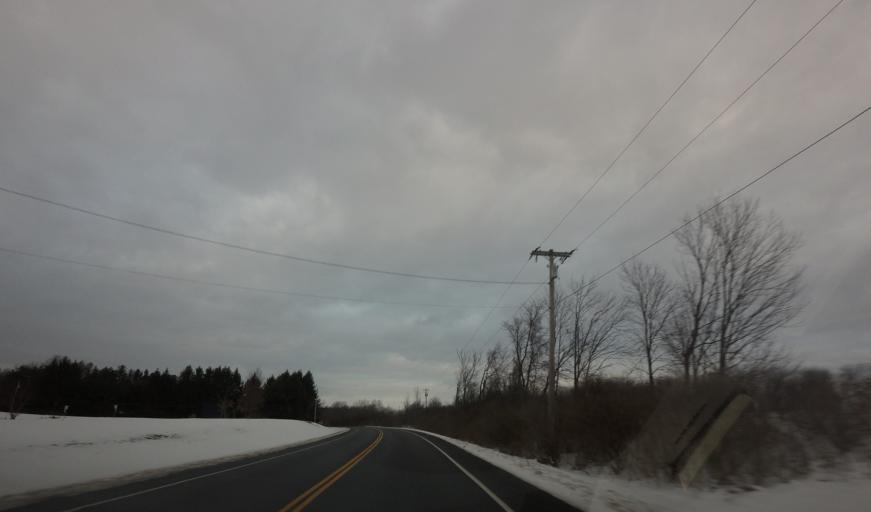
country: US
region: New York
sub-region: Tompkins County
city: Dryden
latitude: 42.5370
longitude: -76.3019
